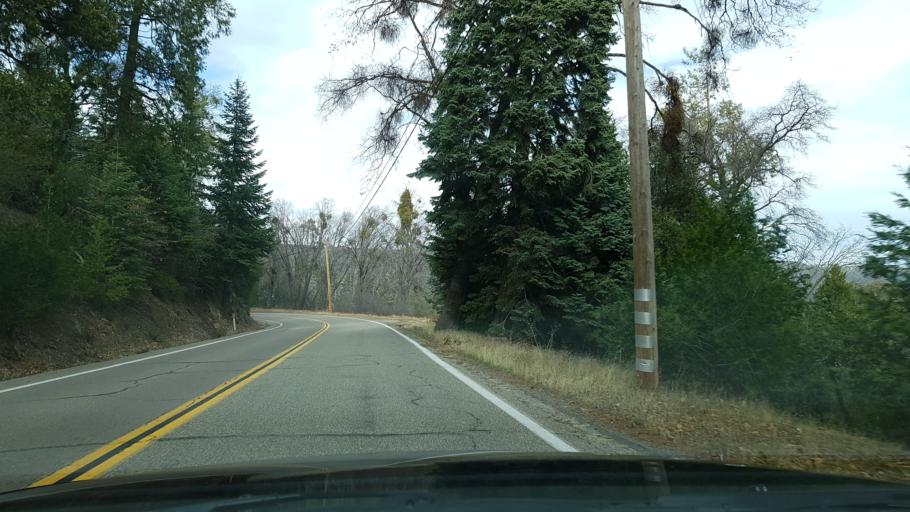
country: US
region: California
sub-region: Riverside County
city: Aguanga
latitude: 33.3176
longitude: -116.8637
